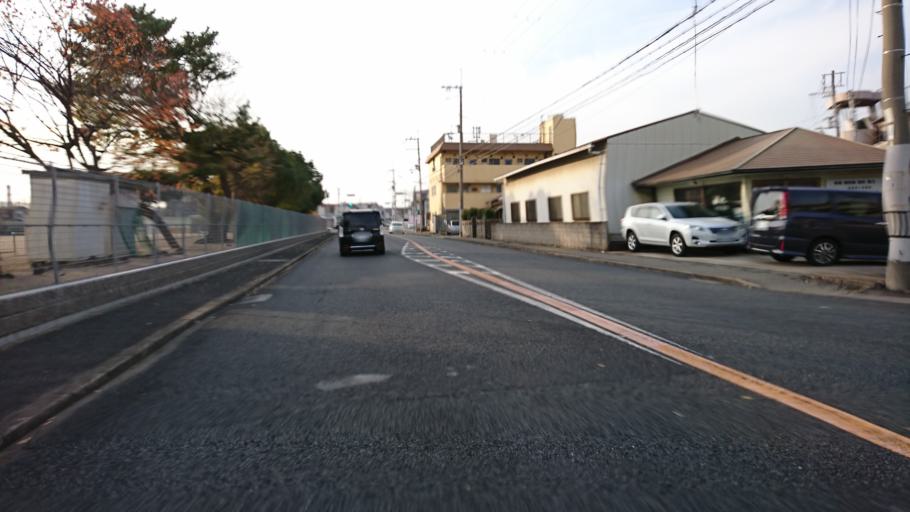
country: JP
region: Hyogo
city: Kakogawacho-honmachi
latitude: 34.7277
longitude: 134.8431
